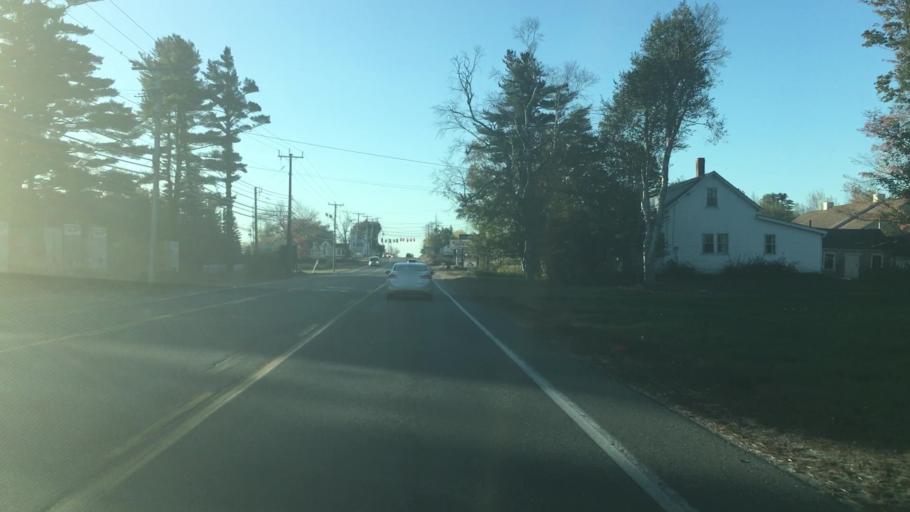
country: US
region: Maine
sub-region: Hancock County
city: Ellsworth
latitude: 44.5221
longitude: -68.3967
